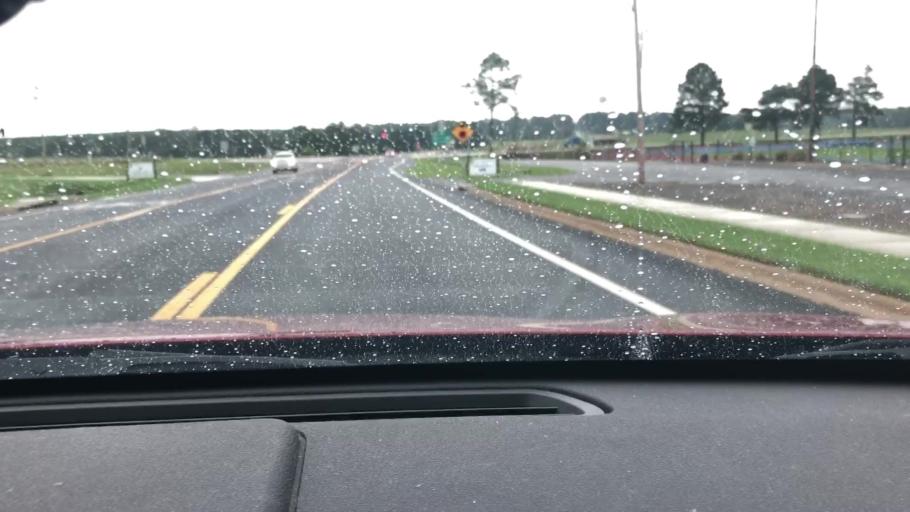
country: US
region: Arkansas
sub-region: Columbia County
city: Magnolia
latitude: 33.2952
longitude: -93.2361
